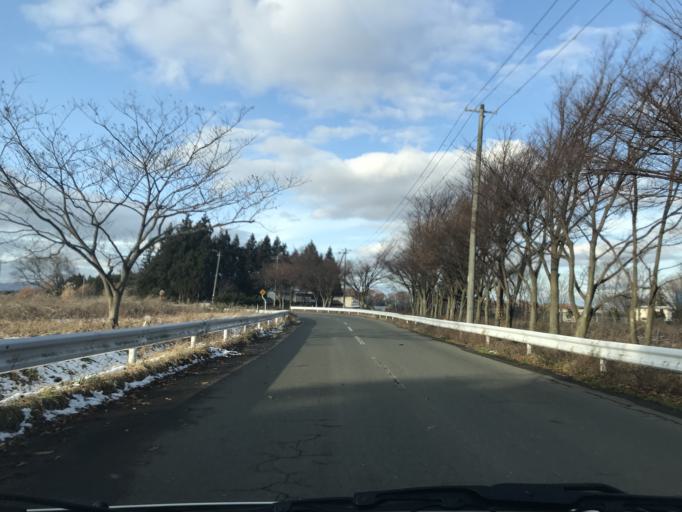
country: JP
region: Iwate
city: Kitakami
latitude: 39.2543
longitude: 141.0324
